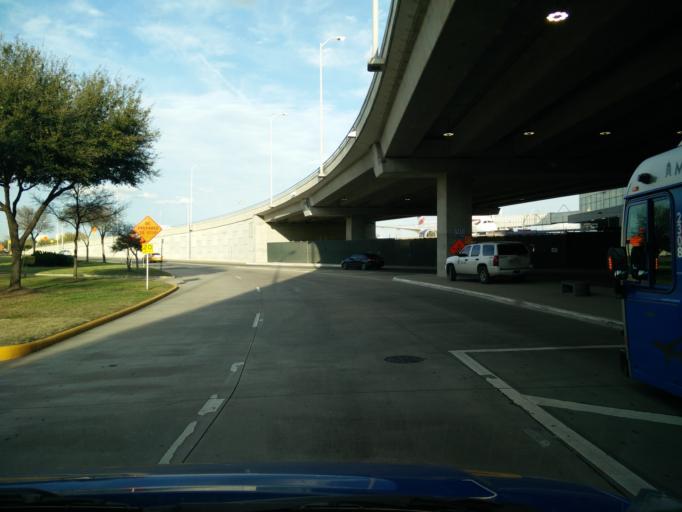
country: US
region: Texas
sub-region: Travis County
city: Hornsby Bend
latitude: 30.2028
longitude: -97.6657
